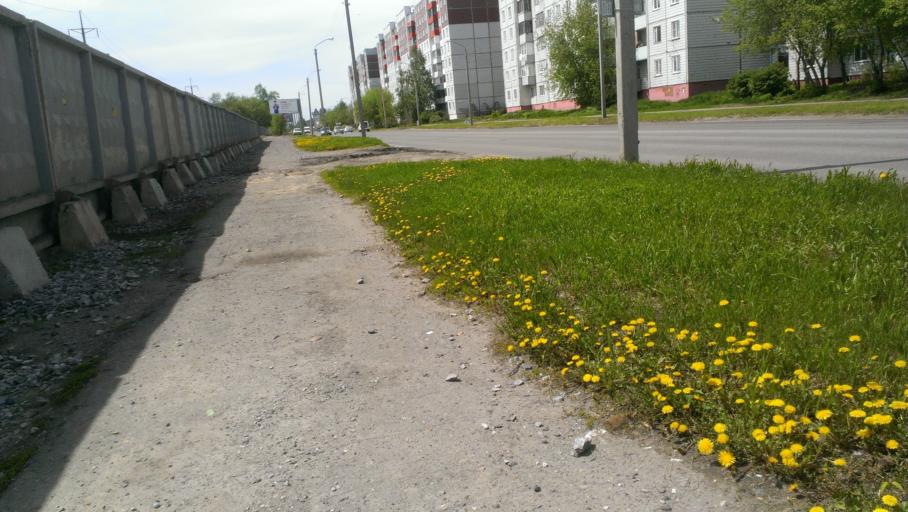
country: RU
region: Altai Krai
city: Novosilikatnyy
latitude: 53.3565
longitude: 83.6651
